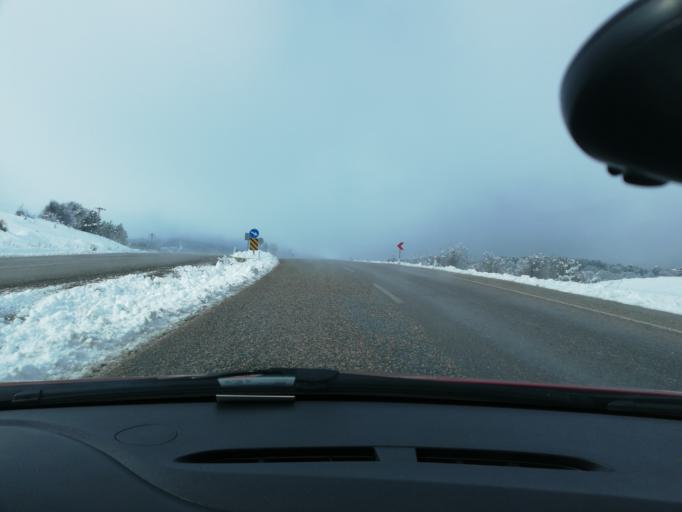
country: TR
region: Kastamonu
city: Ihsangazi
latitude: 41.3070
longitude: 33.5724
